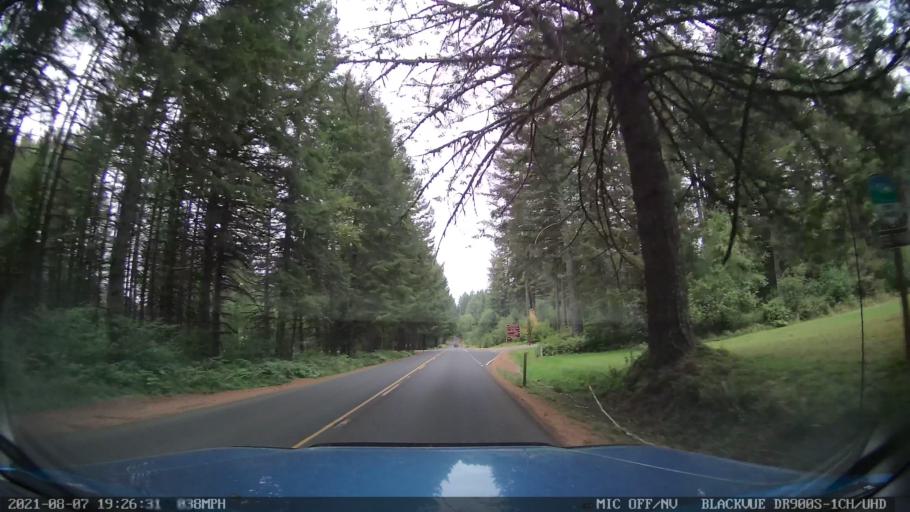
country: US
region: Oregon
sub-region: Linn County
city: Lyons
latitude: 44.8728
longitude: -122.6517
